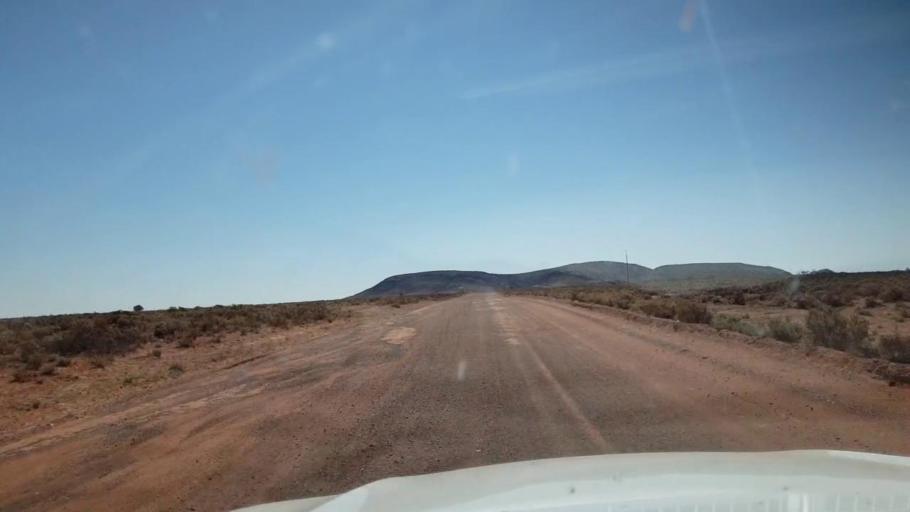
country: AU
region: South Australia
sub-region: Whyalla
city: Whyalla
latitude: -32.7078
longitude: 137.1385
